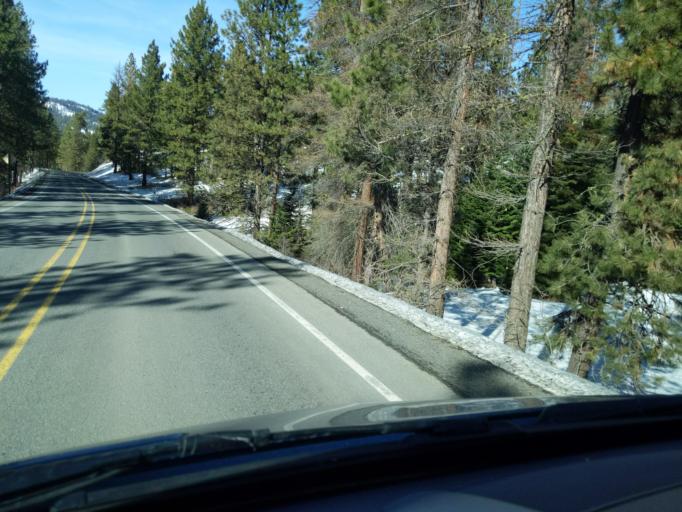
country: US
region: Oregon
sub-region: Grant County
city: John Day
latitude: 44.9154
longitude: -119.0086
